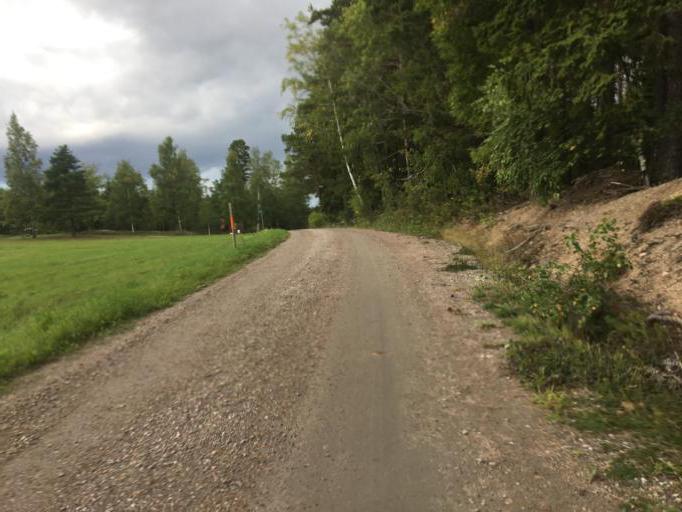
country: SE
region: Soedermanland
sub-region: Eskilstuna Kommun
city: Arla
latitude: 59.4567
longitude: 16.6800
